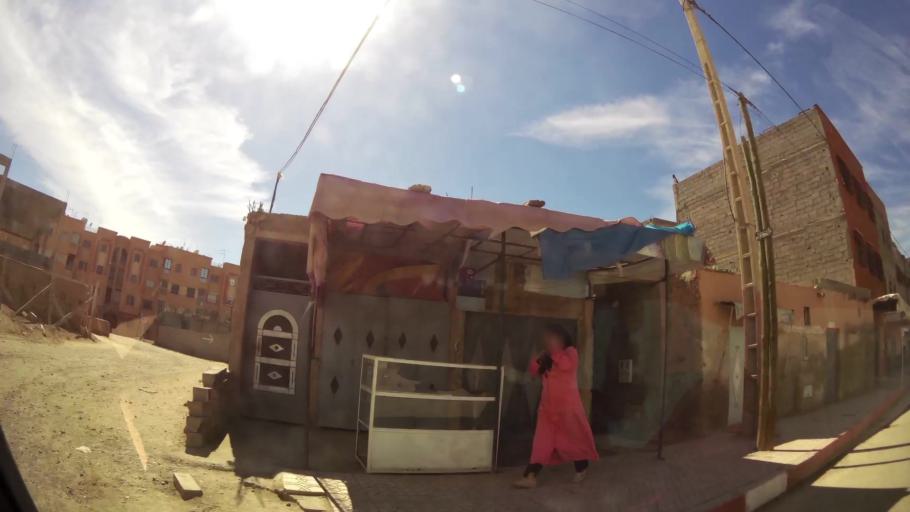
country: MA
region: Marrakech-Tensift-Al Haouz
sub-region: Marrakech
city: Marrakesh
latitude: 31.6776
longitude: -8.0168
